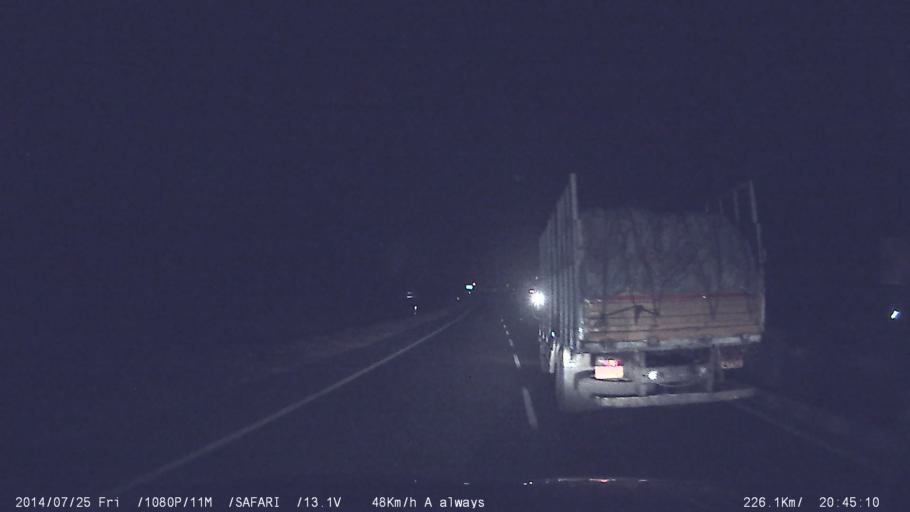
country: IN
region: Tamil Nadu
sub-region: Salem
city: Konganapuram
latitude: 11.5078
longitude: 77.9171
